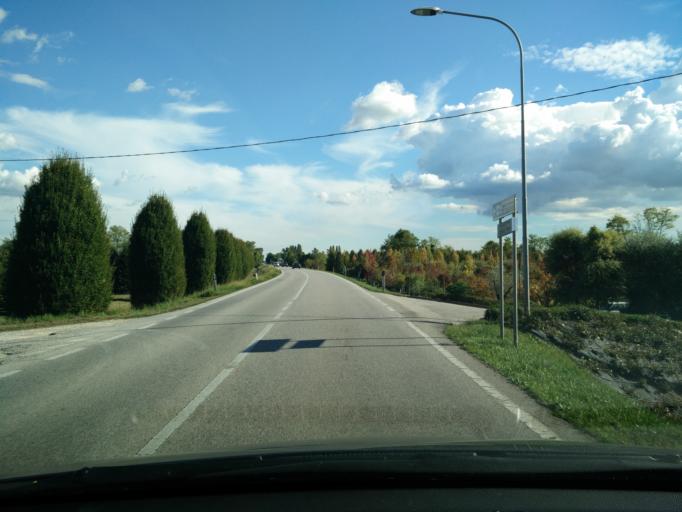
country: IT
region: Veneto
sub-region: Provincia di Treviso
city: Saletto-San Bartolomeo
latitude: 45.7199
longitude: 12.4056
